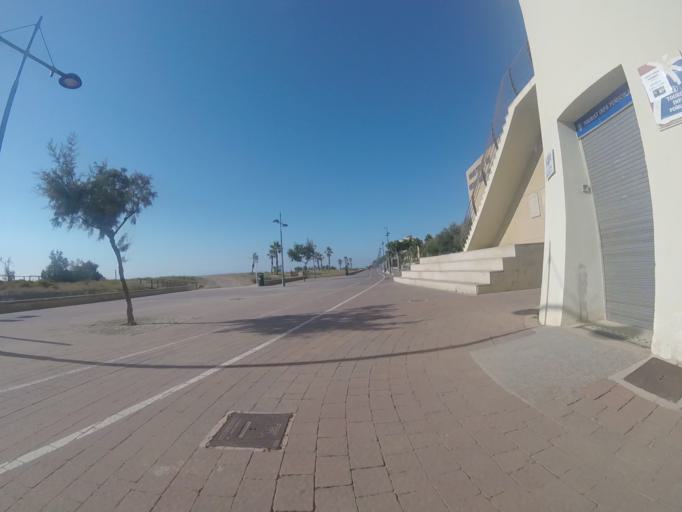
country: ES
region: Valencia
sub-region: Provincia de Castello
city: Peniscola
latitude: 40.3837
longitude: 0.4093
